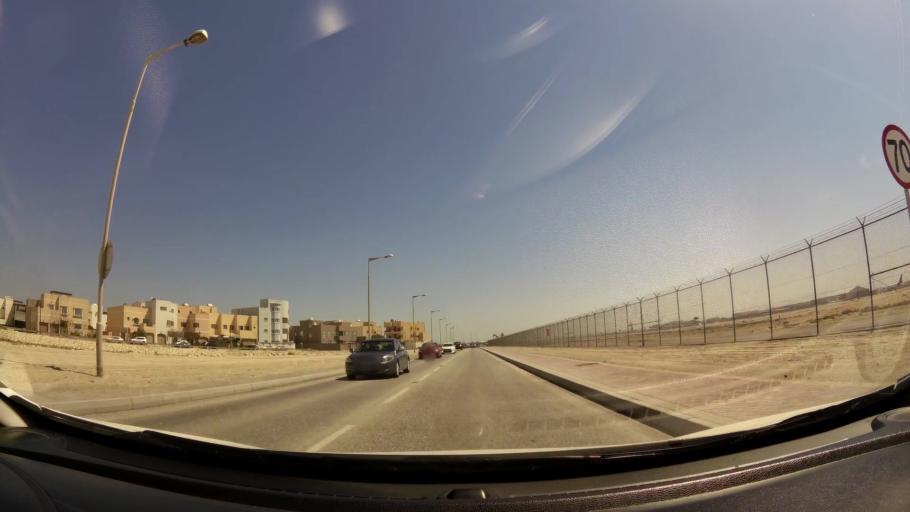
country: BH
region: Muharraq
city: Al Muharraq
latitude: 26.2827
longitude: 50.6165
